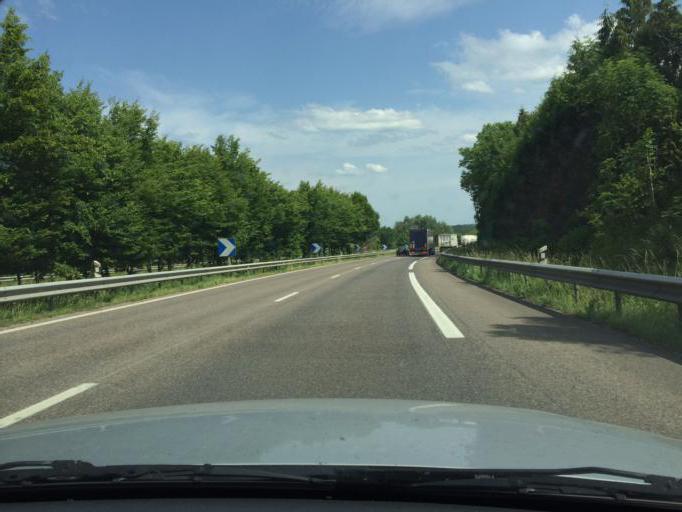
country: FR
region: Lorraine
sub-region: Departement de la Meuse
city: Vacon
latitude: 48.7043
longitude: 5.5284
